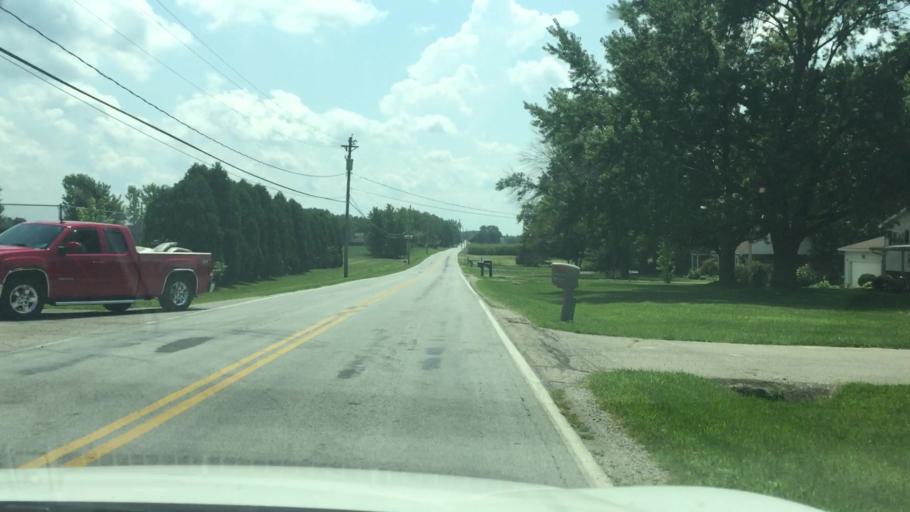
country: US
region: Ohio
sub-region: Clark County
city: Lisbon
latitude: 39.9401
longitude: -83.6820
